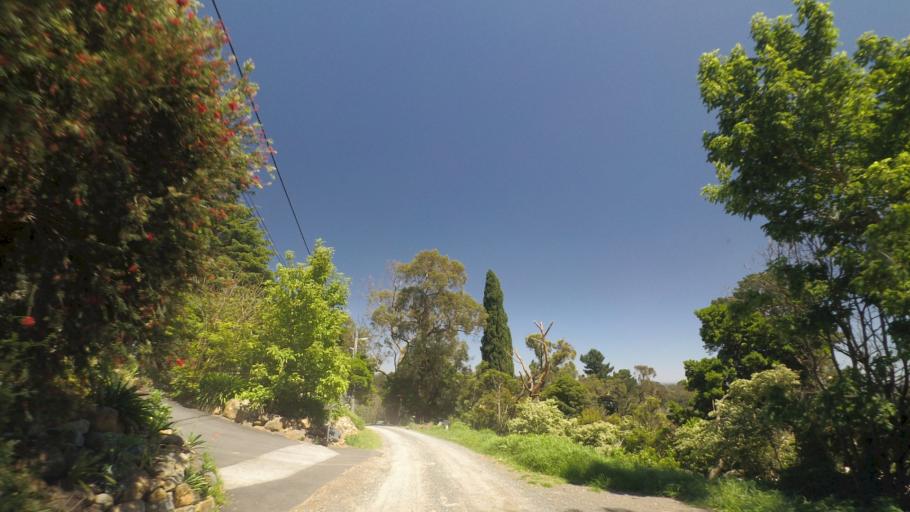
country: AU
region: Victoria
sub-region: Yarra Ranges
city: Montrose
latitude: -37.8115
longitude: 145.3497
